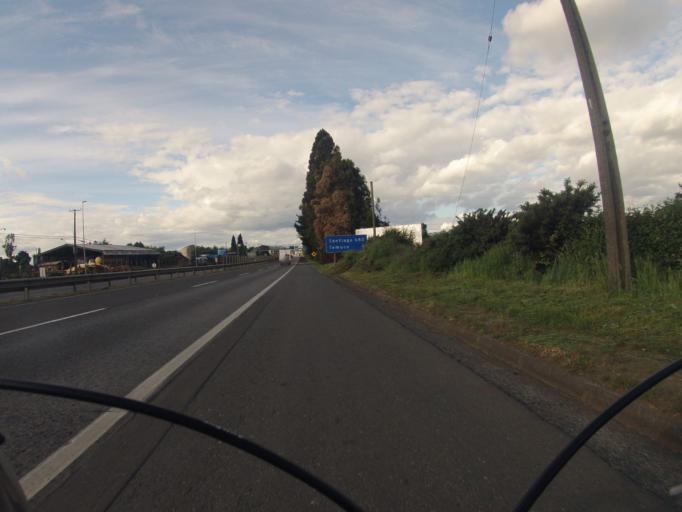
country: CL
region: Araucania
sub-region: Provincia de Cautin
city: Temuco
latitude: -38.7978
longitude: -72.6223
